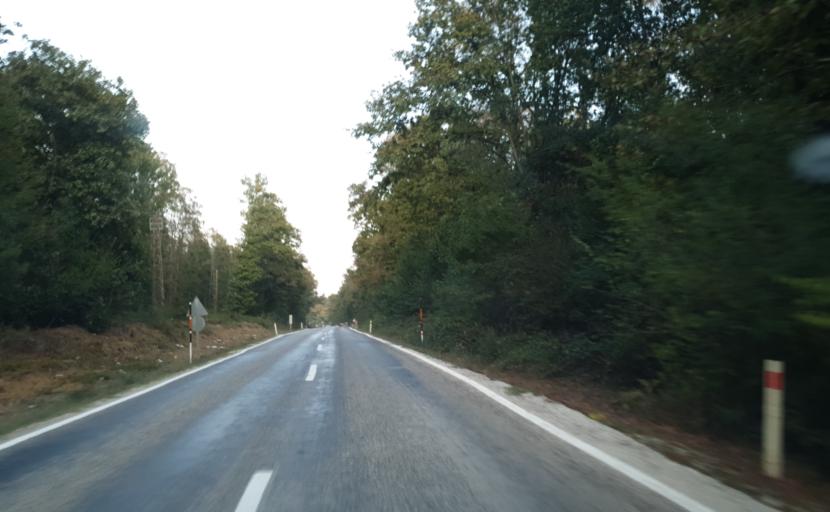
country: TR
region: Kirklareli
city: Igneada
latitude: 41.8715
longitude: 27.9299
